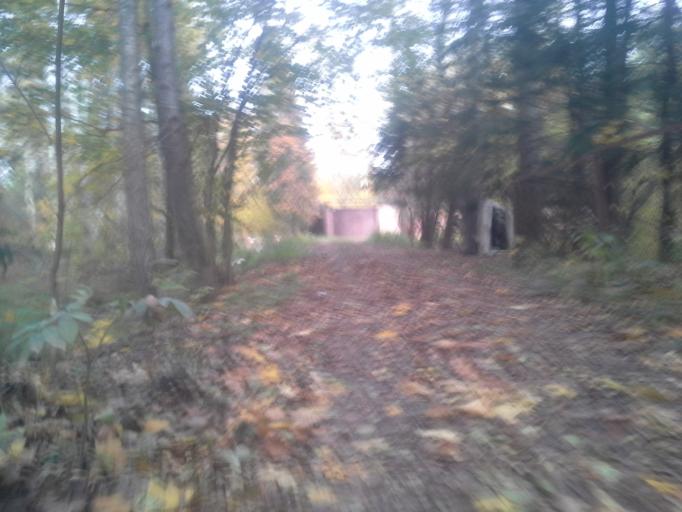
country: RU
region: Moskovskaya
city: Krasnoznamensk
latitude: 55.5811
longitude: 37.0232
